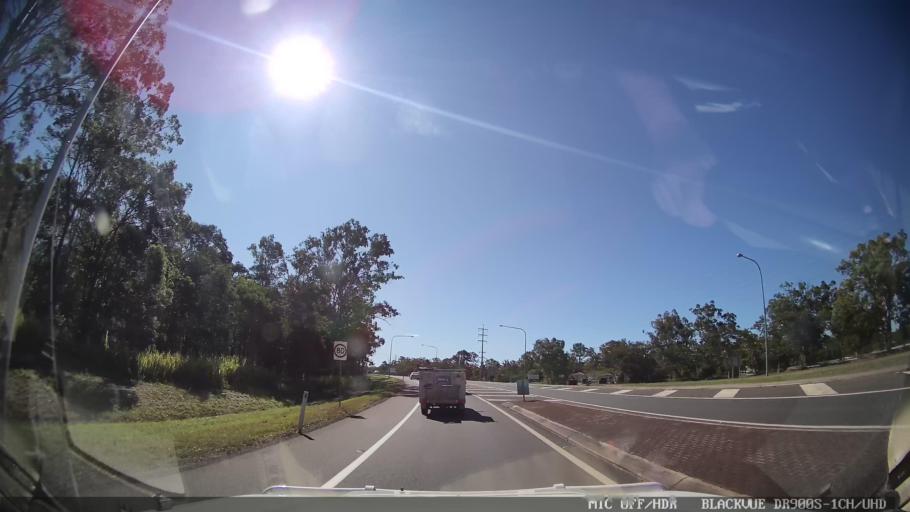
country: AU
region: Queensland
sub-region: Fraser Coast
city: Maryborough
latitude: -25.5134
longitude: 152.6709
